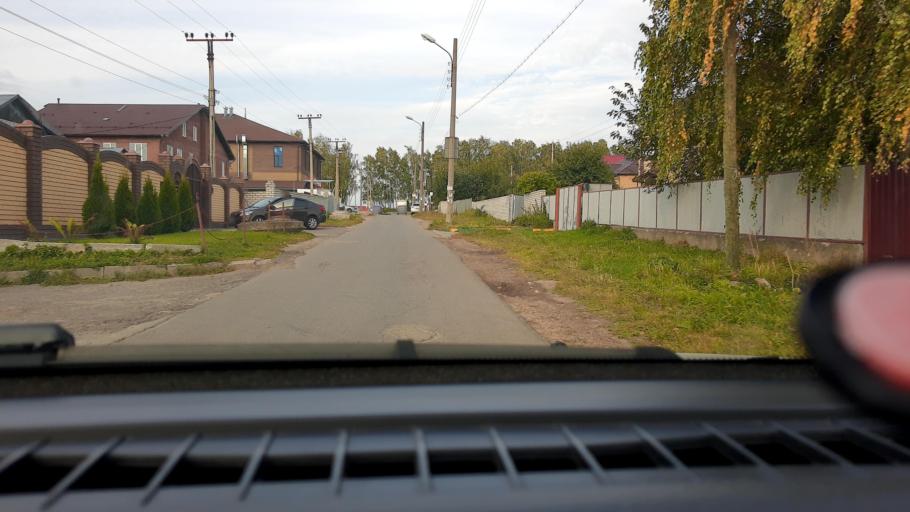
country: RU
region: Nizjnij Novgorod
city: Nizhniy Novgorod
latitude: 56.2135
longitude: 43.9590
